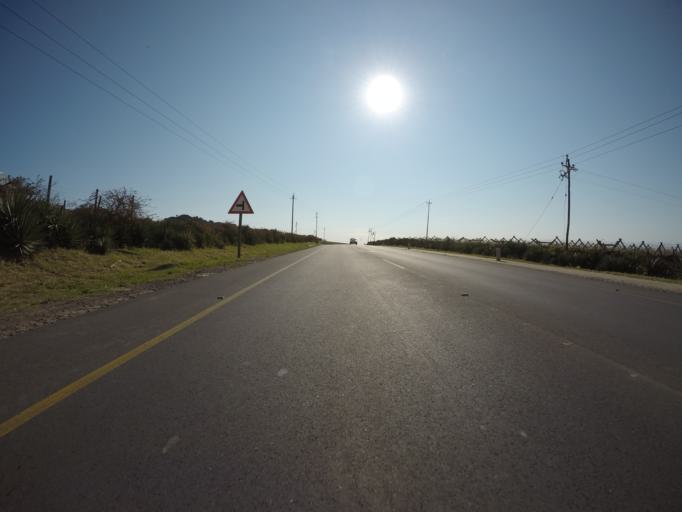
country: ZA
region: Western Cape
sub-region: Cape Winelands District Municipality
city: Noorder-Paarl
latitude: -33.6774
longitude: 18.9385
